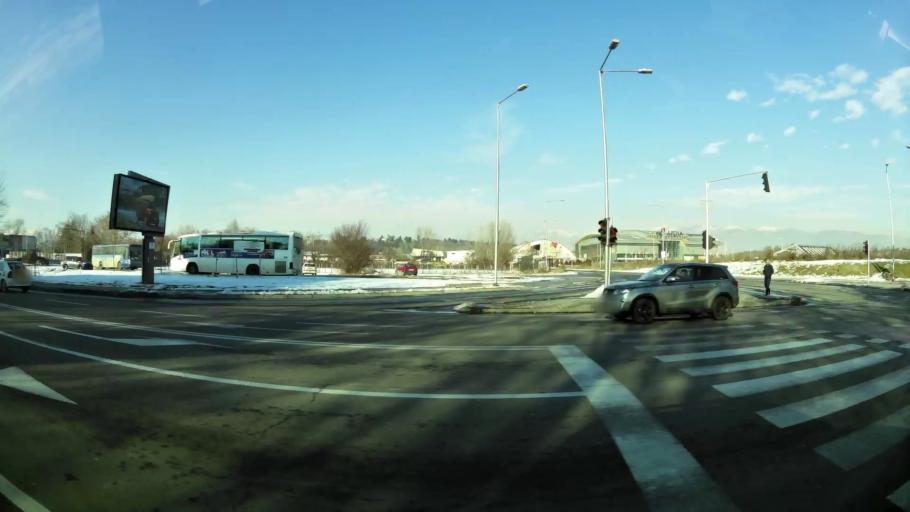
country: MK
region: Karpos
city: Skopje
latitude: 42.0072
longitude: 21.4024
